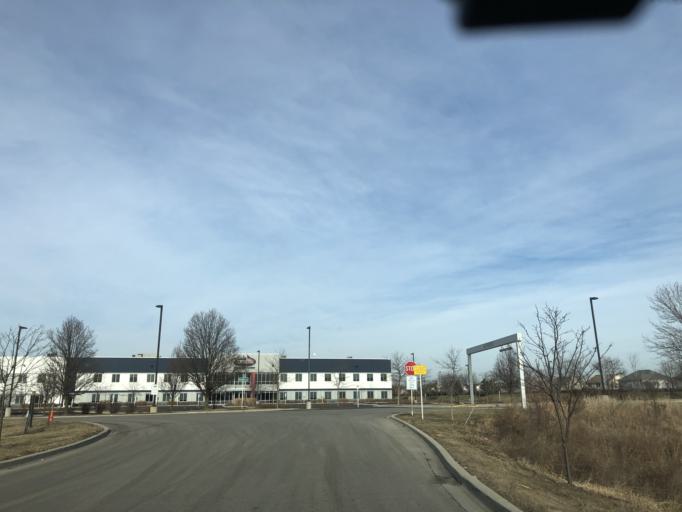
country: US
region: Illinois
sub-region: DuPage County
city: Woodridge
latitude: 41.7134
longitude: -88.0283
